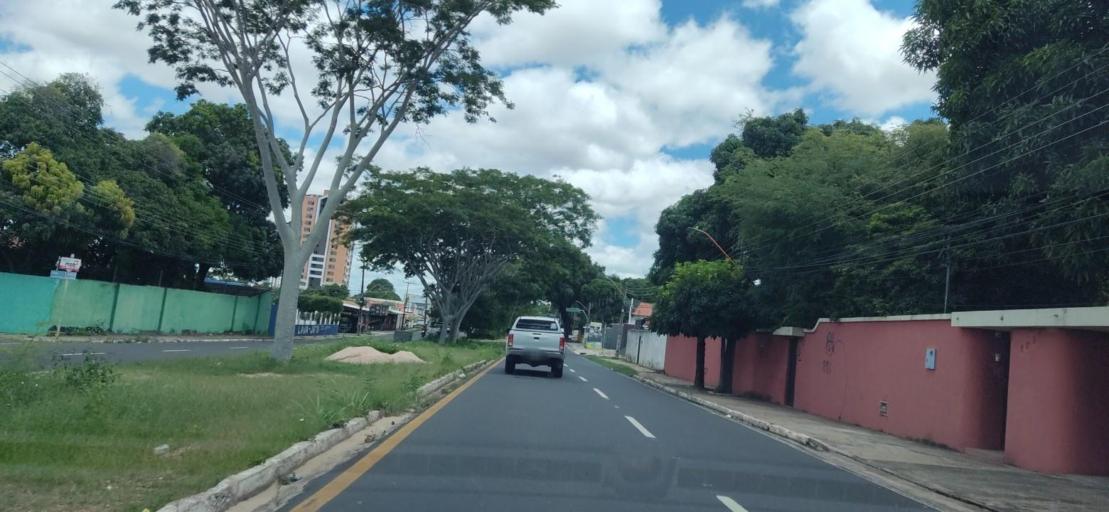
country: BR
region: Piaui
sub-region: Teresina
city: Teresina
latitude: -5.0649
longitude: -42.7673
